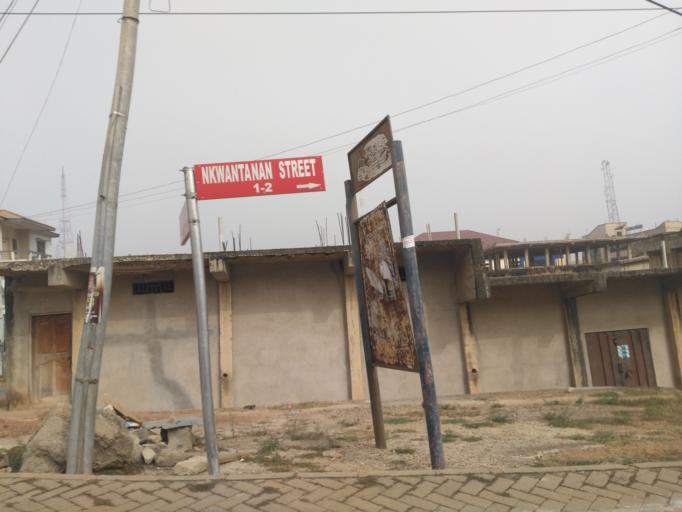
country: GH
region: Ashanti
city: Kumasi
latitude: 6.6877
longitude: -1.6199
